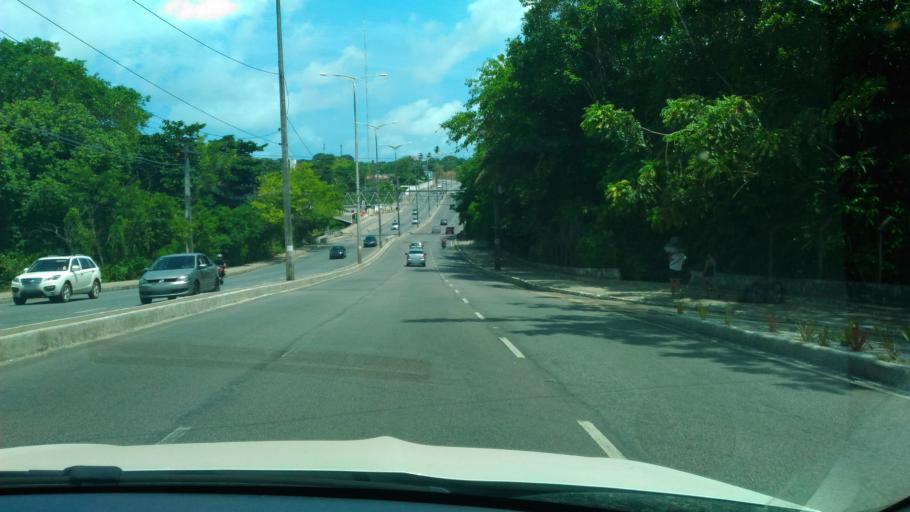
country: BR
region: Paraiba
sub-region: Joao Pessoa
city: Joao Pessoa
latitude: -7.1350
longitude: -34.8594
